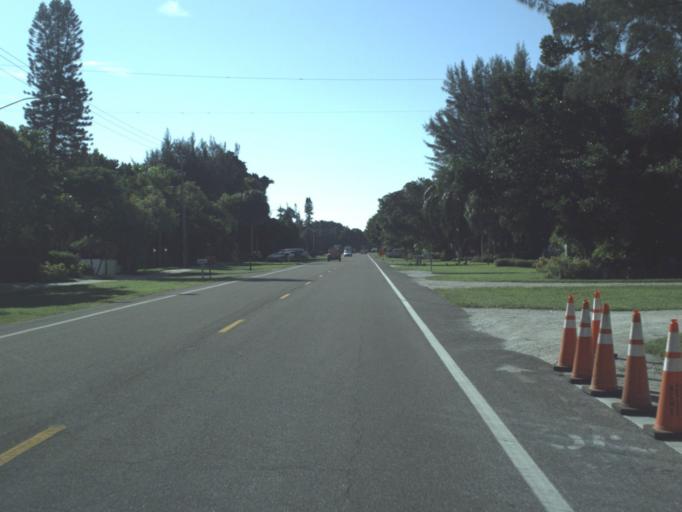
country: US
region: Florida
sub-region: Manatee County
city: Longboat Key
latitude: 27.4077
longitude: -82.6545
